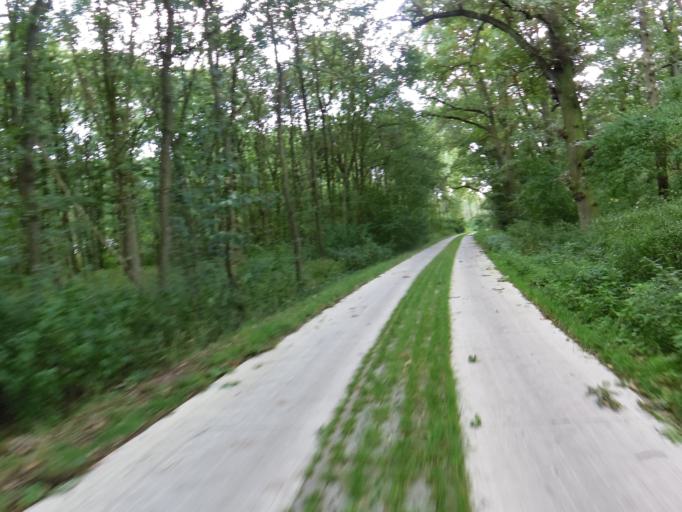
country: DE
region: Saxony-Anhalt
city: Barby
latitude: 51.9876
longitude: 11.8973
